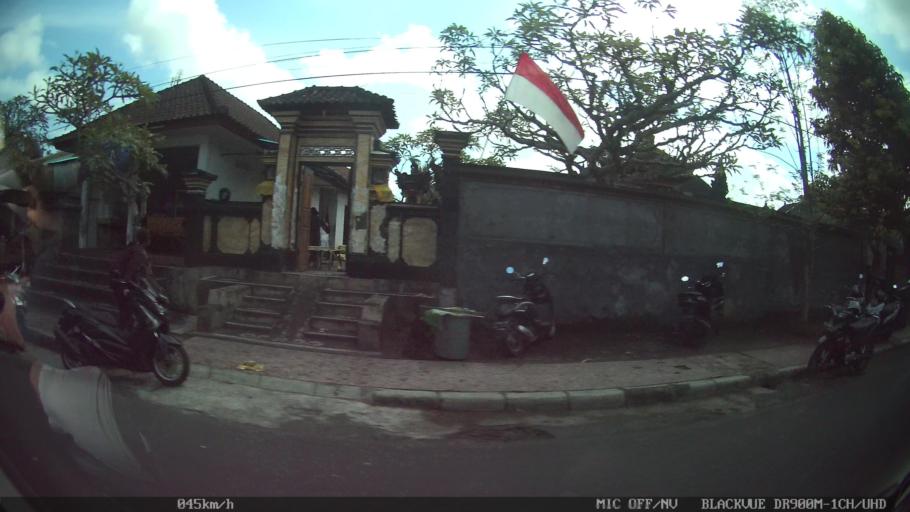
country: ID
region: Bali
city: Banjar Kelodan
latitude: -8.5337
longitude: 115.3287
